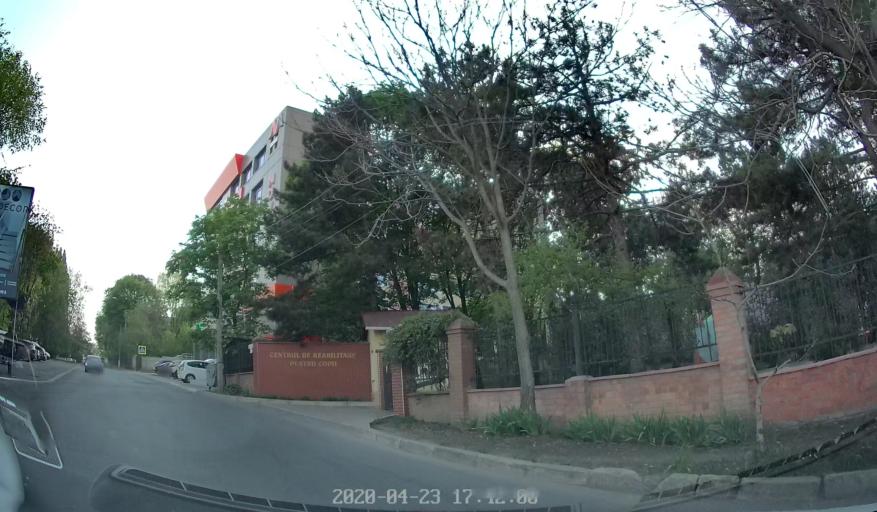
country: MD
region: Chisinau
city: Chisinau
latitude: 46.9888
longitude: 28.8350
